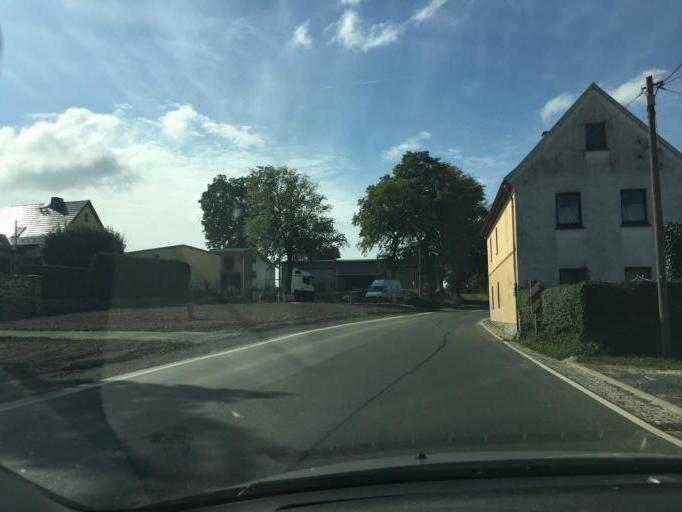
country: DE
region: Thuringia
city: Mittelpollnitz
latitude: 50.7346
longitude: 11.9122
